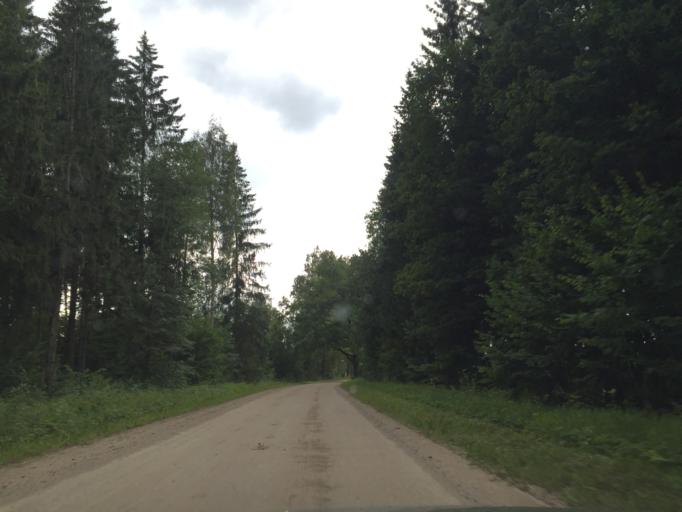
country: LV
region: Malpils
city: Malpils
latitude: 56.9468
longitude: 24.9985
